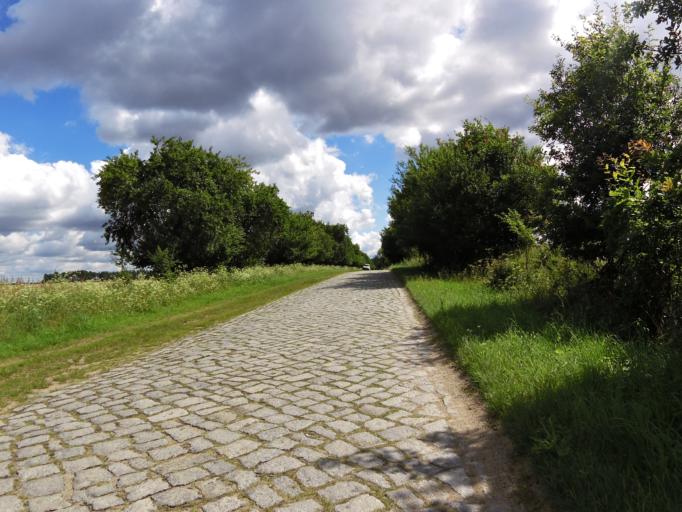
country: DE
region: Brandenburg
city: Lychen
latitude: 53.2683
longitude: 13.3562
